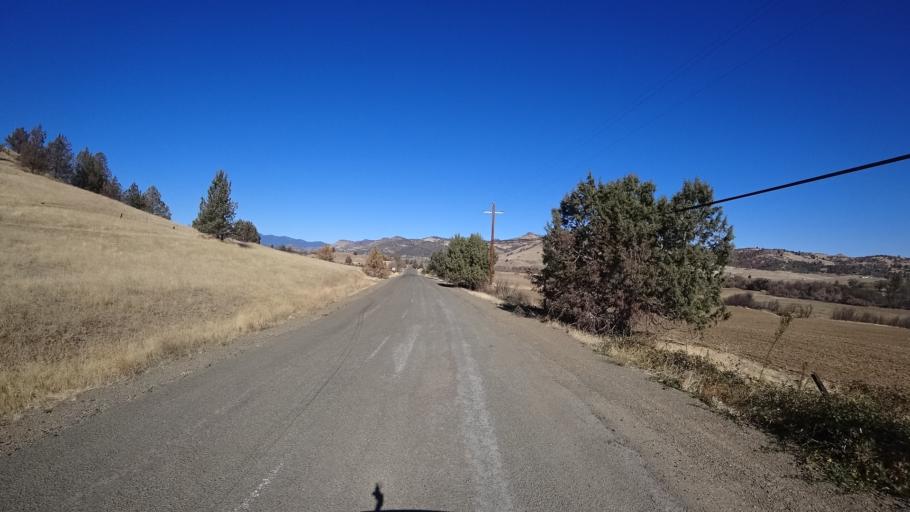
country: US
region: California
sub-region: Siskiyou County
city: Montague
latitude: 41.8911
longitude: -122.5498
